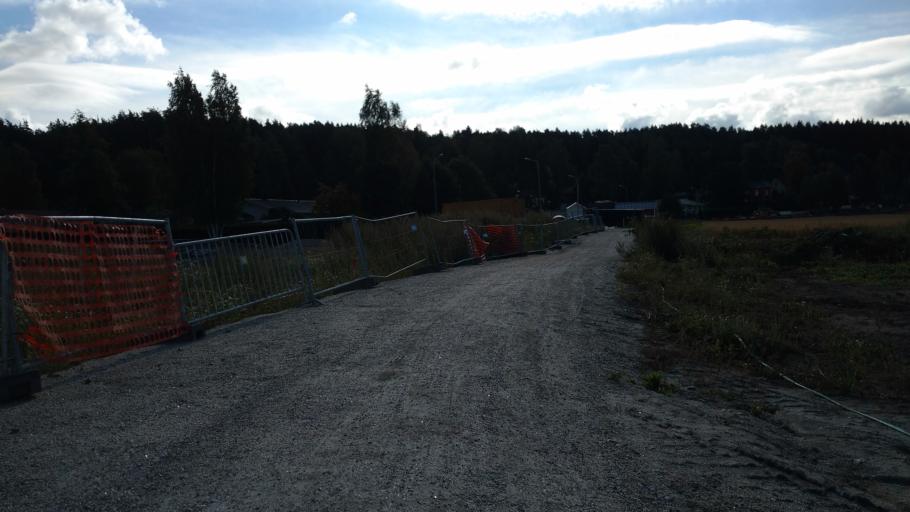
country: FI
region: Varsinais-Suomi
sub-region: Salo
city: Salo
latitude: 60.3734
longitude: 23.1690
